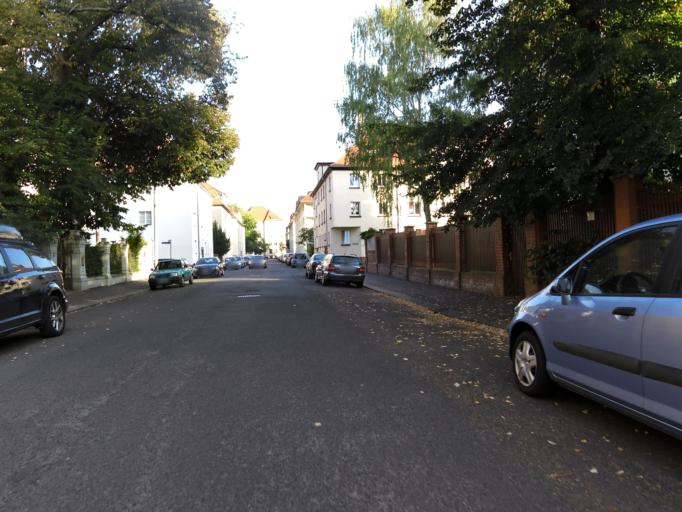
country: DE
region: Saxony
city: Leipzig
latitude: 51.3427
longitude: 12.3274
